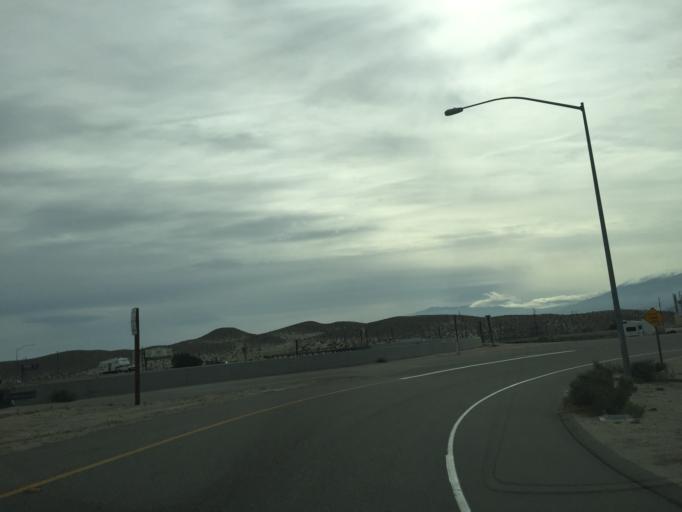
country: US
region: California
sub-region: Riverside County
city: Garnet
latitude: 33.9057
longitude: -116.5442
